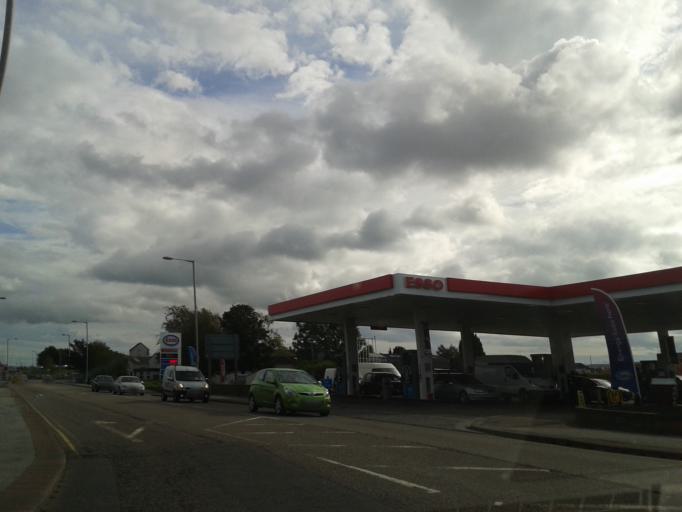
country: GB
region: Scotland
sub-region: Moray
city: Elgin
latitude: 57.6474
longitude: -3.2952
